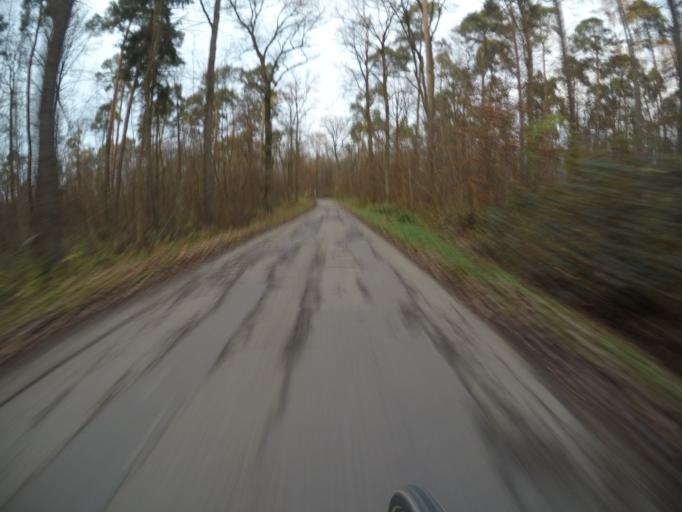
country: DE
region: Baden-Wuerttemberg
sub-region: Regierungsbezirk Stuttgart
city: Ostfildern
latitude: 48.7444
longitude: 9.2527
